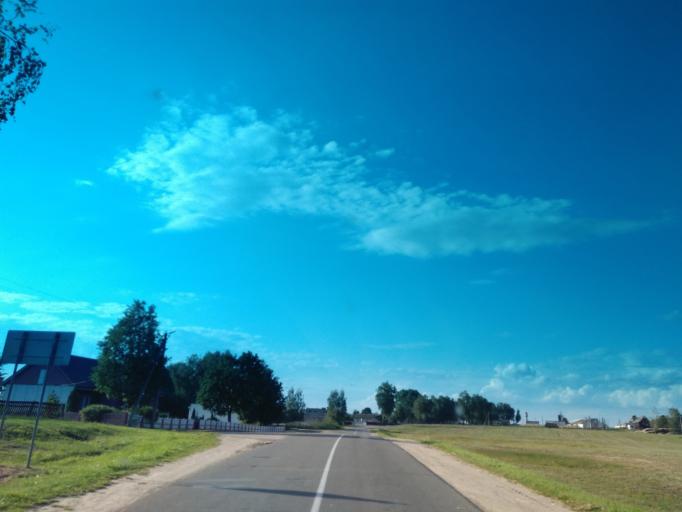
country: BY
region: Minsk
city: Kapyl'
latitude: 53.2584
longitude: 26.9587
